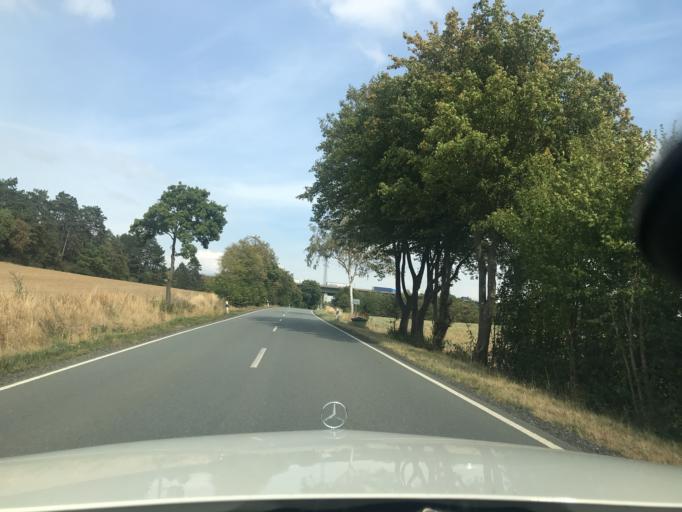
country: DE
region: Hesse
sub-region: Regierungsbezirk Kassel
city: Breuna
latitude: 51.4123
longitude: 9.1570
